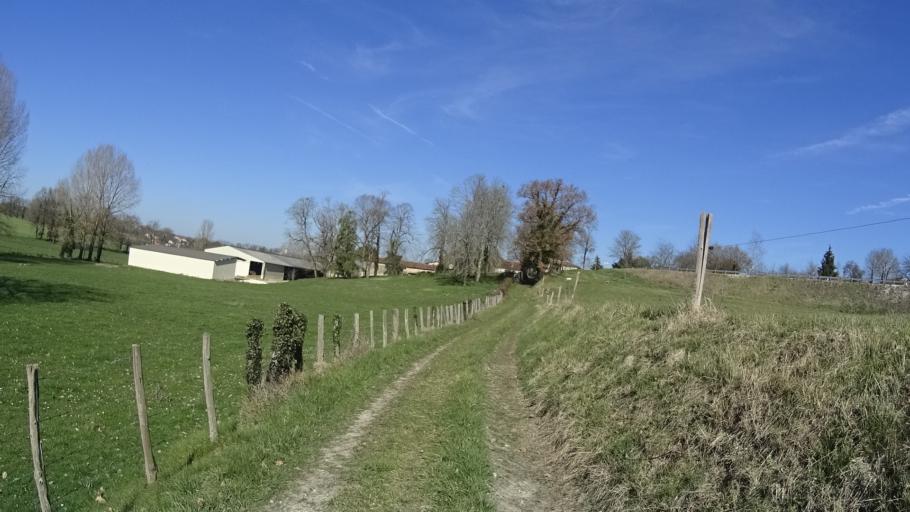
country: FR
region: Aquitaine
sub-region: Departement de la Dordogne
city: Riberac
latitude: 45.2291
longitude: 0.3339
